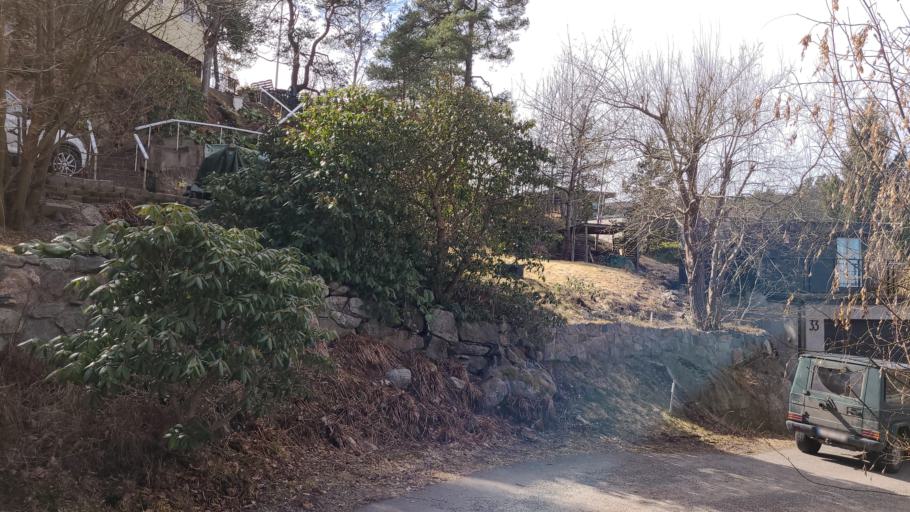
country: SE
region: Stockholm
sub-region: Lidingo
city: Brevik
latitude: 59.3297
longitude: 18.2199
